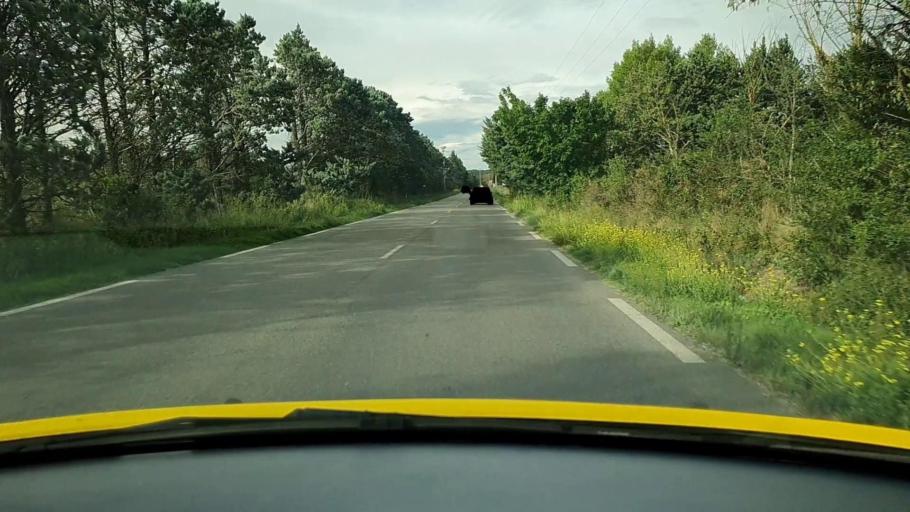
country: FR
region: Languedoc-Roussillon
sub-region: Departement du Gard
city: Jonquieres-Saint-Vincent
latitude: 43.7837
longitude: 4.5646
